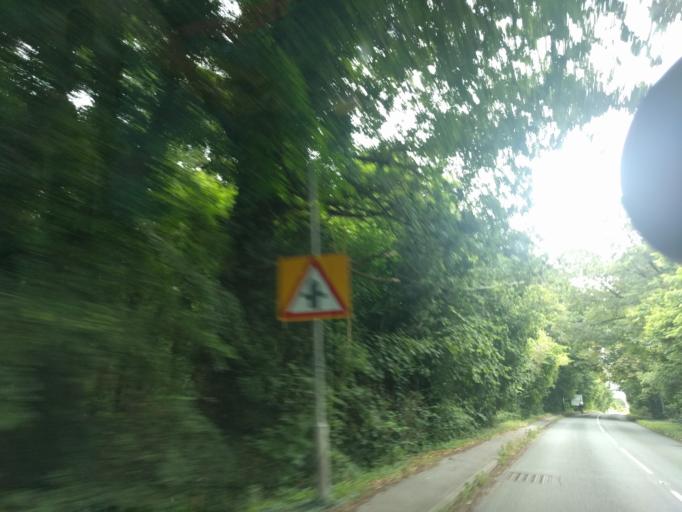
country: GB
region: England
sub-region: Wiltshire
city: Erlestoke
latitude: 51.2825
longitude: -2.0374
